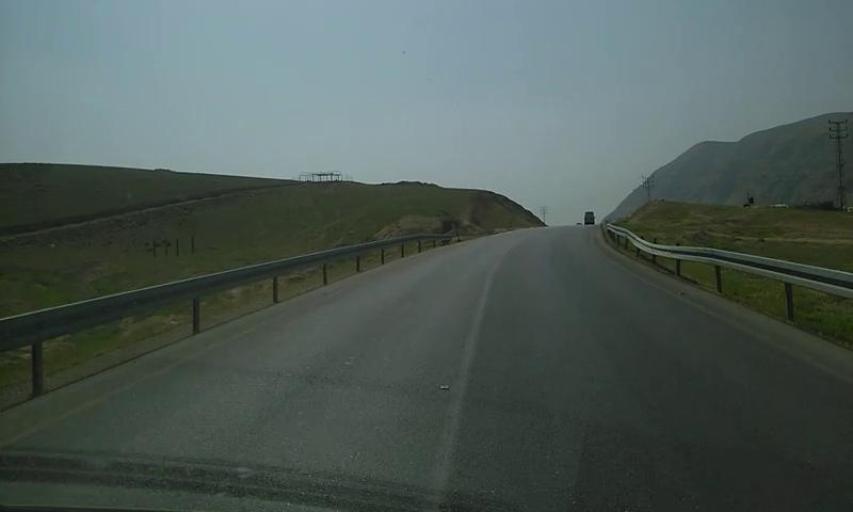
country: PS
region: West Bank
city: An Nuway`imah
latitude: 31.8983
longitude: 35.4278
